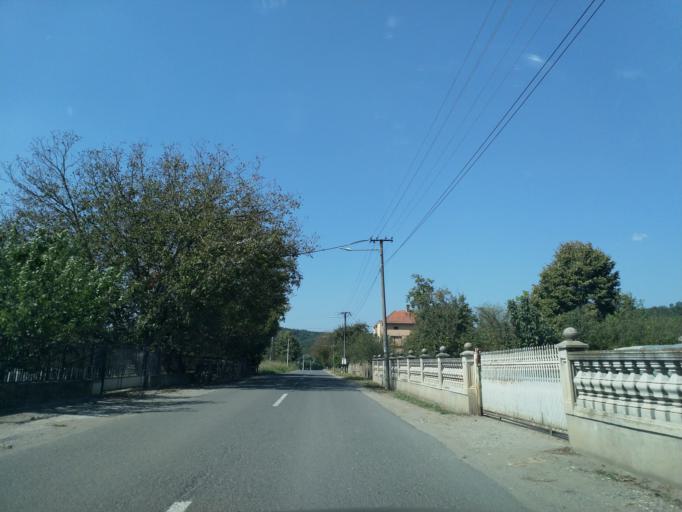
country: RS
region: Central Serbia
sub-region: Rasinski Okrug
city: Krusevac
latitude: 43.6247
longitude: 21.3425
